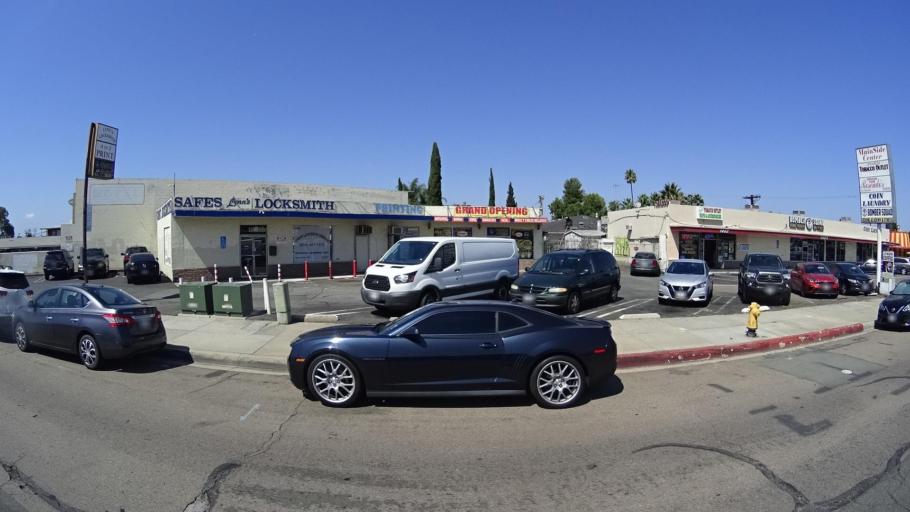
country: US
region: California
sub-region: San Diego County
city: Bostonia
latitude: 32.7992
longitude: -116.9316
